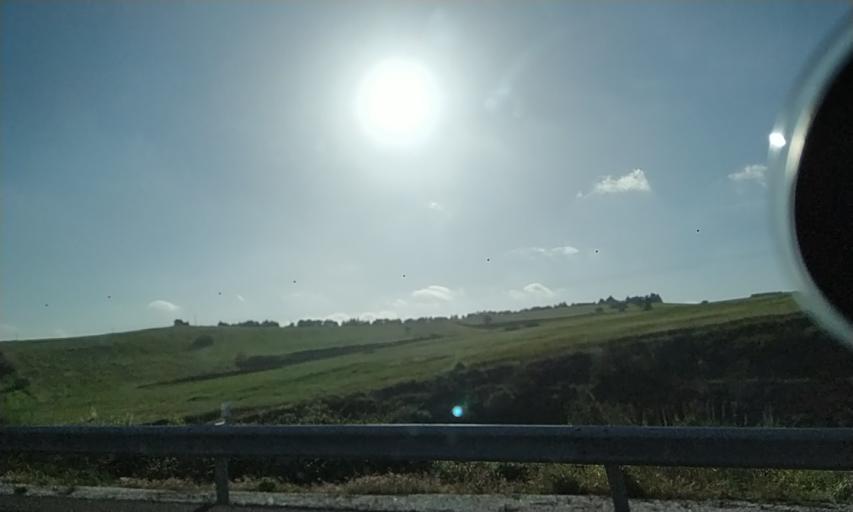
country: PT
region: Lisbon
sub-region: Mafra
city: Milharado
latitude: 38.9798
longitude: -9.2210
